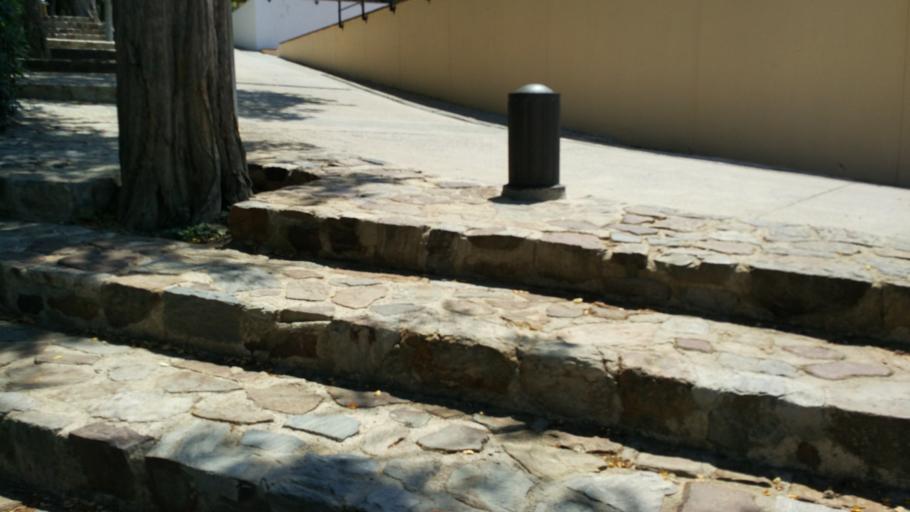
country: ES
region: Catalonia
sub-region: Provincia de Barcelona
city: Sant Just Desvern
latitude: 41.4199
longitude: 2.1002
